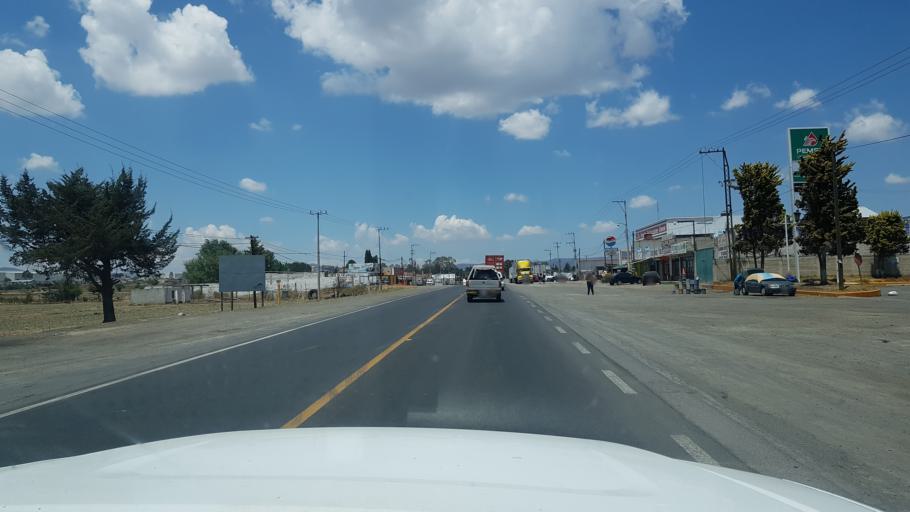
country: MX
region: Hidalgo
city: Calpulalpan
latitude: 19.5868
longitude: -98.5467
